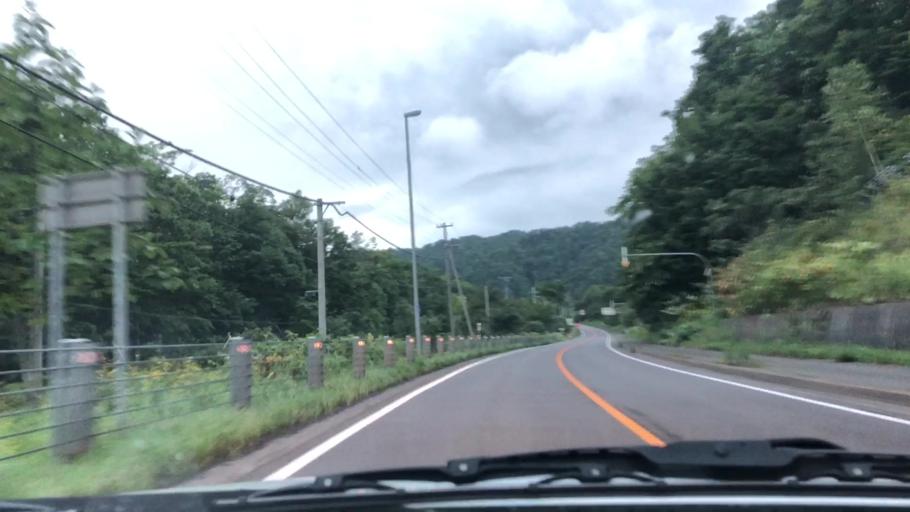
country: JP
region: Hokkaido
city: Chitose
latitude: 42.9137
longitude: 141.9655
